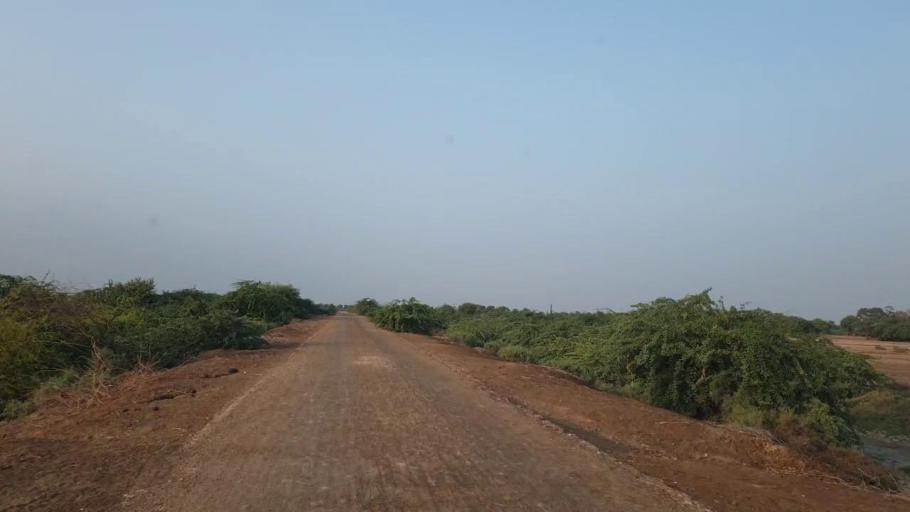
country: PK
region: Sindh
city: Tando Ghulam Ali
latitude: 25.0613
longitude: 68.9605
